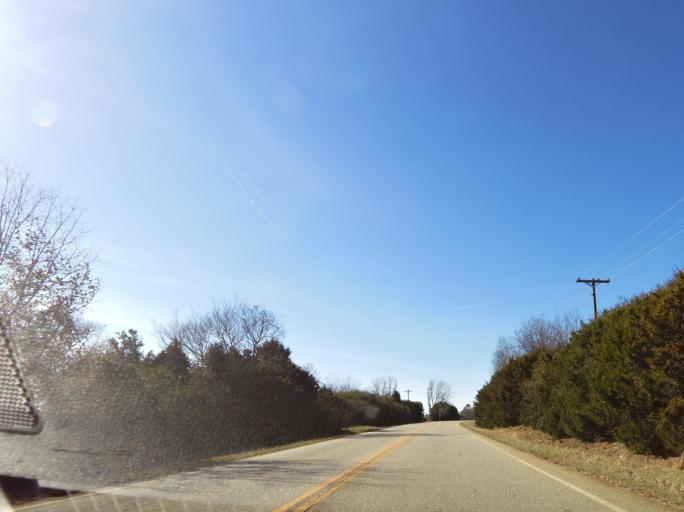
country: US
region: Georgia
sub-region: Crawford County
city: Roberta
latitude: 32.8742
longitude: -84.0656
